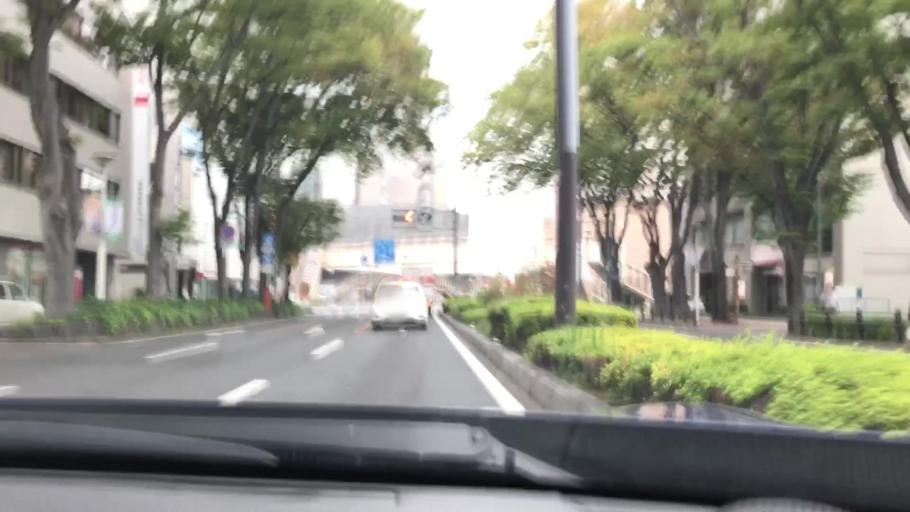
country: JP
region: Gunma
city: Maebashi-shi
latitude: 36.3878
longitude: 139.0725
